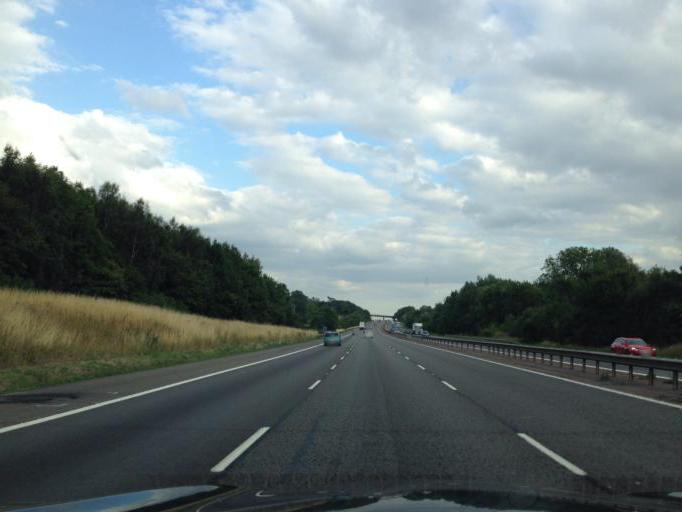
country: GB
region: England
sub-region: Oxfordshire
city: Hanwell
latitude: 52.0955
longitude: -1.3474
